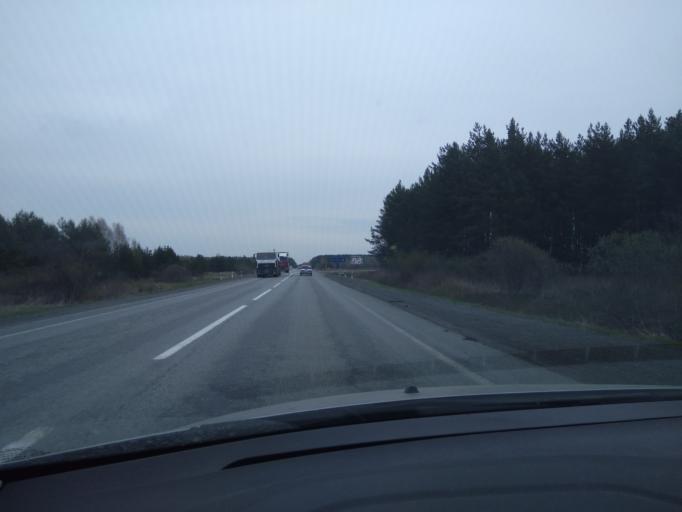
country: RU
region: Sverdlovsk
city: Baraba
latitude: 56.7854
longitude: 61.7544
